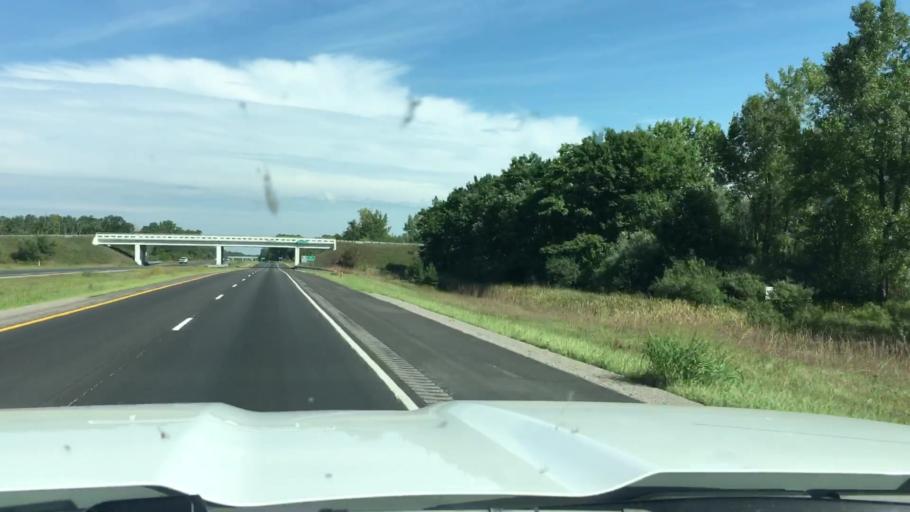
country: US
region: Michigan
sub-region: Saginaw County
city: Freeland
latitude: 43.5664
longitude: -84.1388
